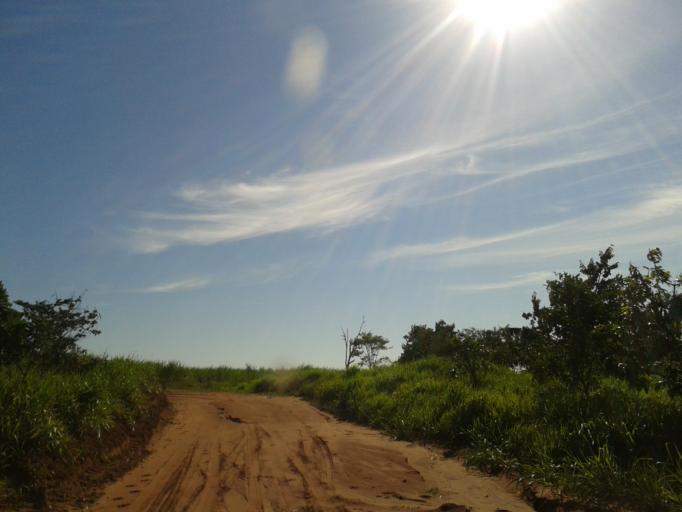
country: BR
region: Minas Gerais
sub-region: Santa Vitoria
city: Santa Vitoria
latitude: -19.1217
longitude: -49.9971
